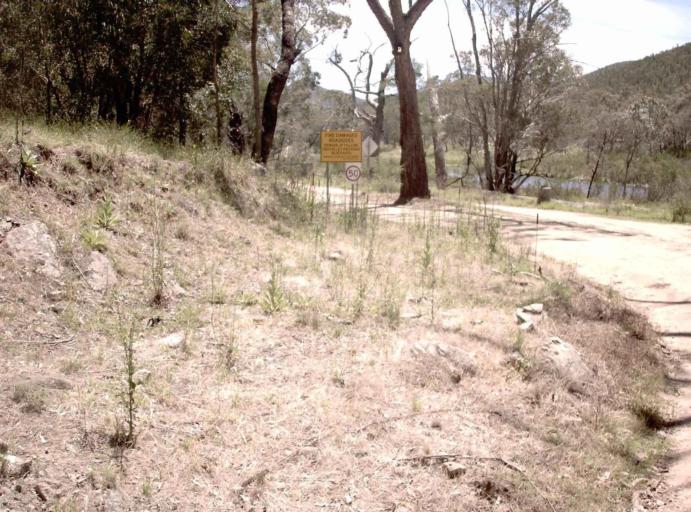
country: AU
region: New South Wales
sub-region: Snowy River
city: Jindabyne
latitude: -36.8886
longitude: 148.4207
